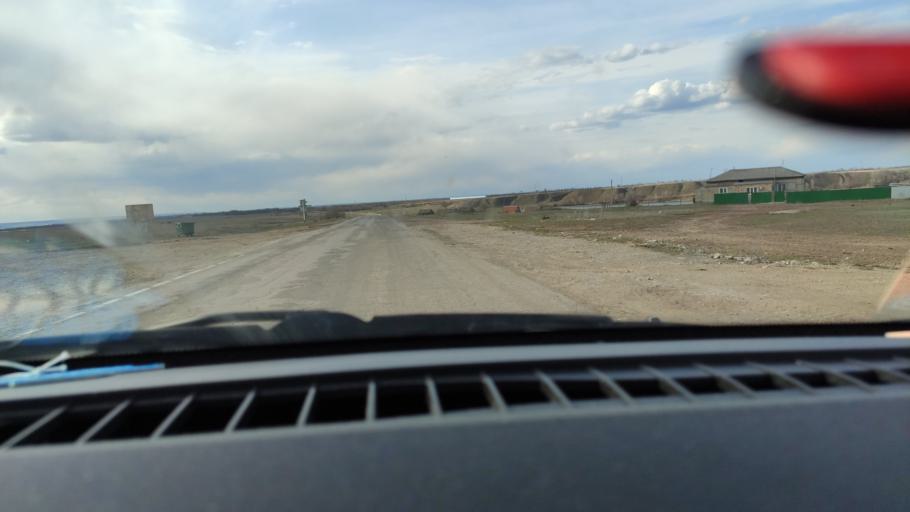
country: RU
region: Saratov
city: Rovnoye
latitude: 51.0299
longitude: 46.0885
